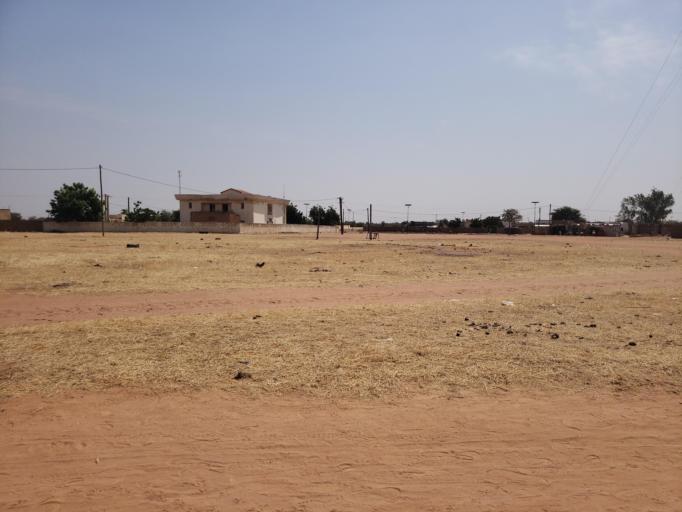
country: SN
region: Matam
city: Ranerou
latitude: 15.3000
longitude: -13.9581
